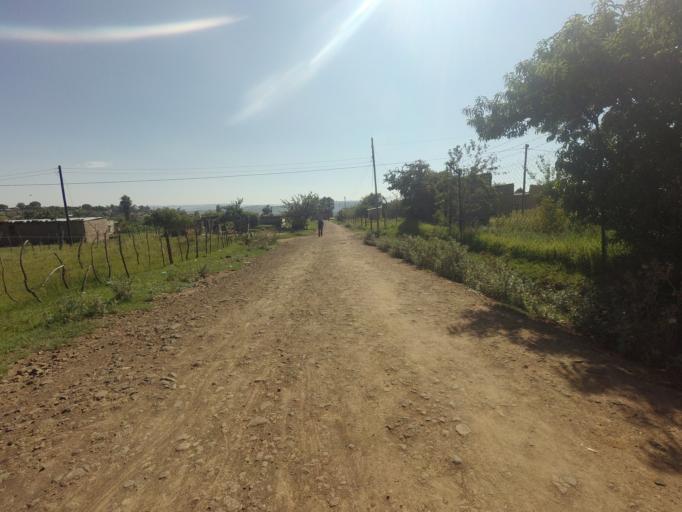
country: LS
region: Berea
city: Teyateyaneng
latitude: -29.1474
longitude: 27.7514
